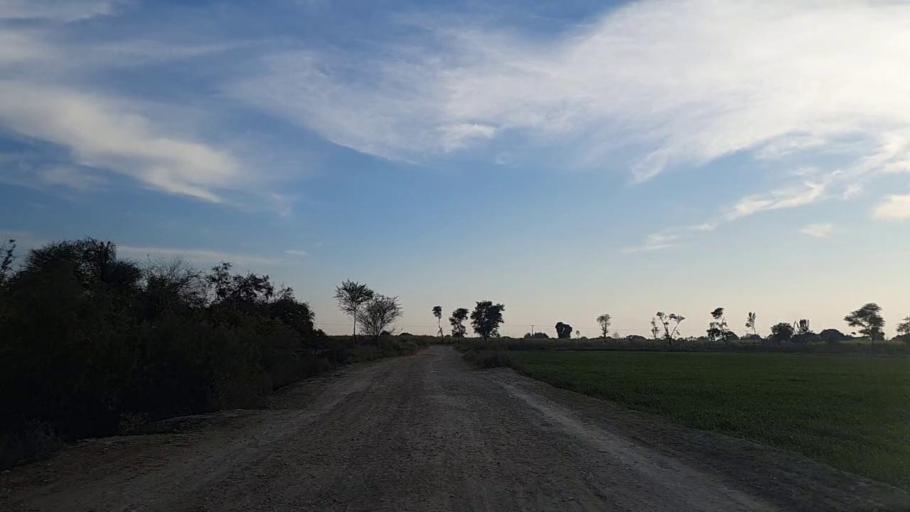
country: PK
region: Sindh
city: Bandhi
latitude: 26.5520
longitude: 68.2808
